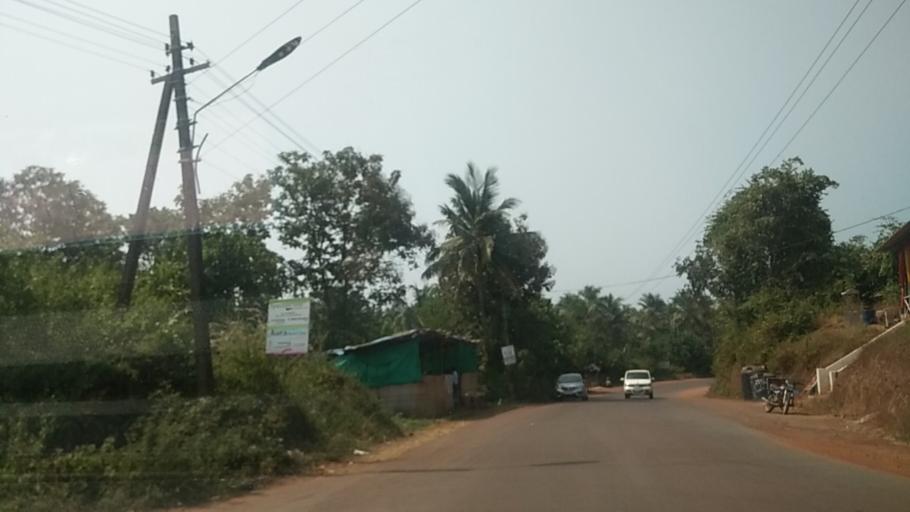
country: IN
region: Goa
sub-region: North Goa
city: Arambol
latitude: 15.6703
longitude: 73.7124
